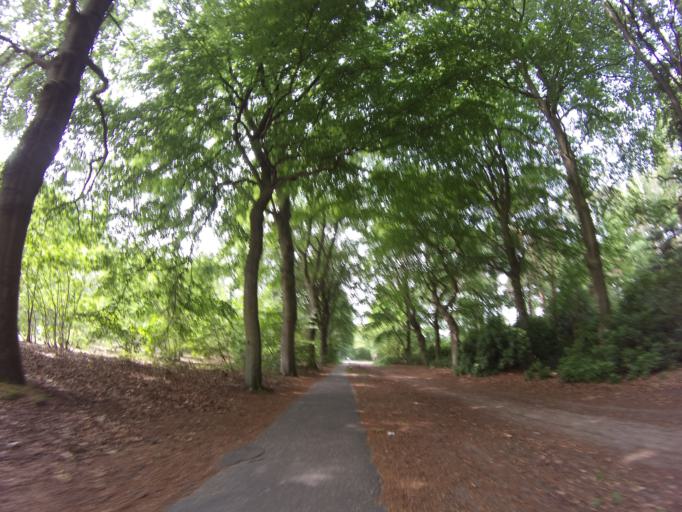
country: NL
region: Utrecht
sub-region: Gemeente Zeist
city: Zeist
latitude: 52.1056
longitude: 5.2728
